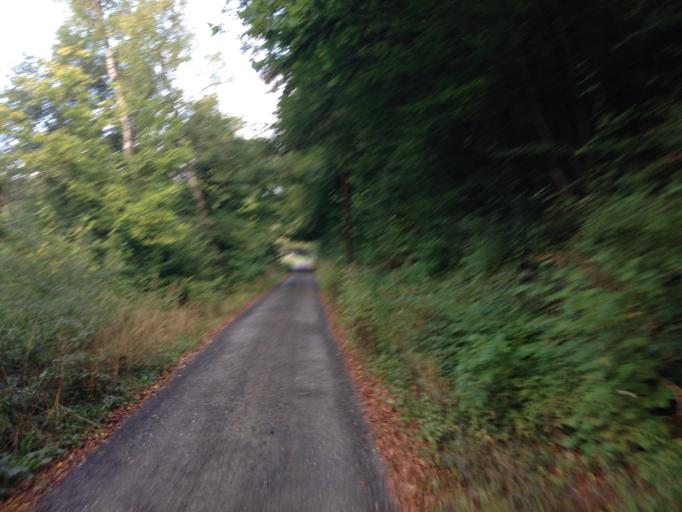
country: DE
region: Hesse
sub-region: Regierungsbezirk Giessen
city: Heuchelheim
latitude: 50.6368
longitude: 8.5661
